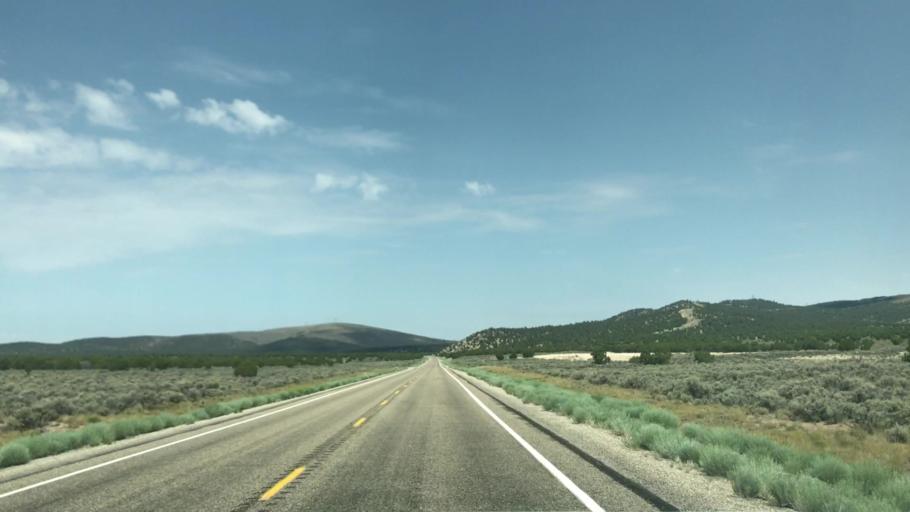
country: US
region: Nevada
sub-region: White Pine County
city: Ely
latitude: 39.3723
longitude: -115.0586
